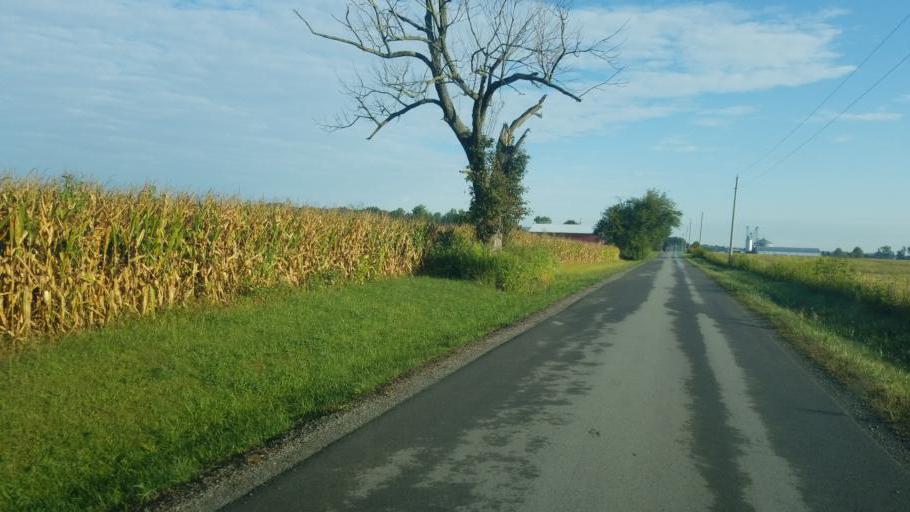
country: US
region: Ohio
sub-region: Morrow County
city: Cardington
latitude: 40.5987
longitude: -82.9380
